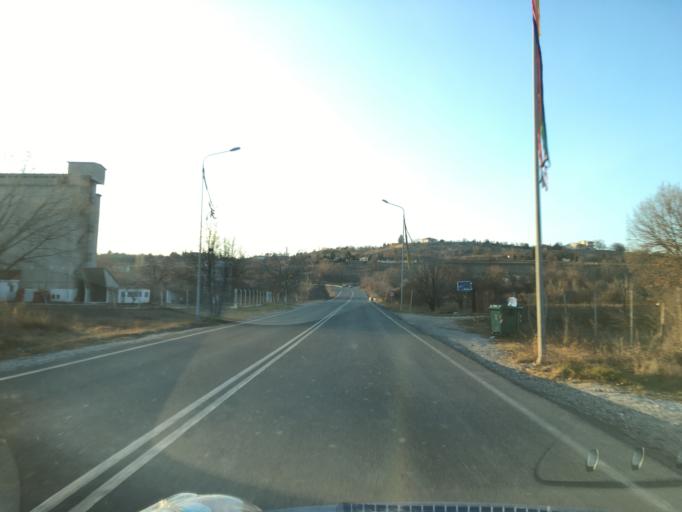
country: GR
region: West Macedonia
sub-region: Nomos Kozanis
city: Kozani
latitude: 40.2877
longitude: 21.7762
